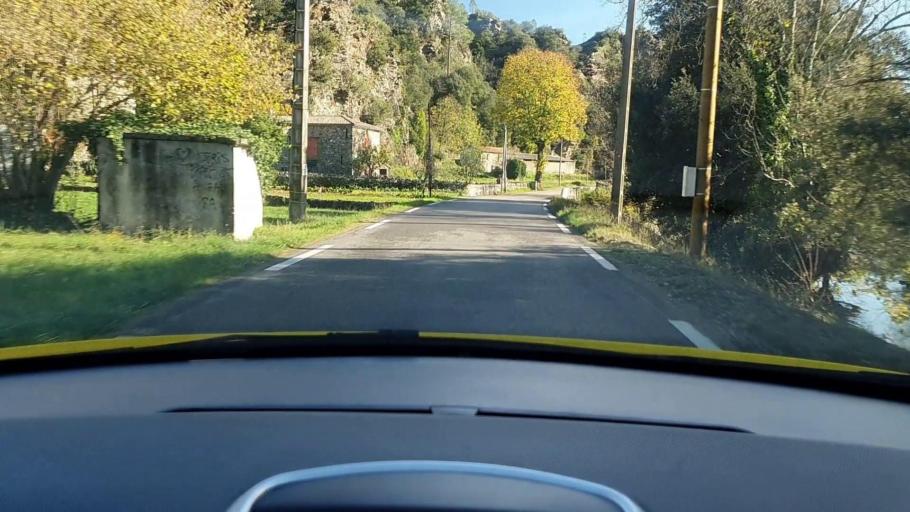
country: FR
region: Languedoc-Roussillon
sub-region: Departement du Gard
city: Valleraugue
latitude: 44.1377
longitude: 3.7498
